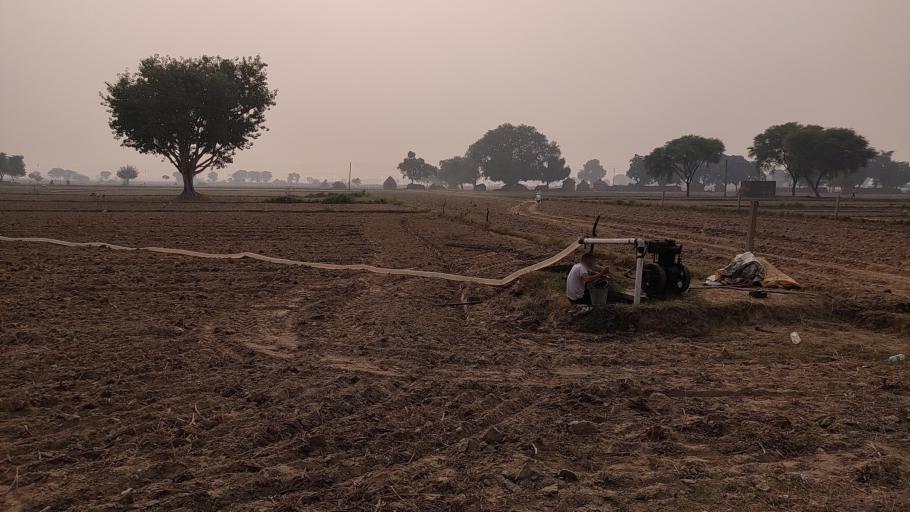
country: IN
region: Uttar Pradesh
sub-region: Mathura
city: Vrindavan
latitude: 27.5539
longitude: 77.7148
